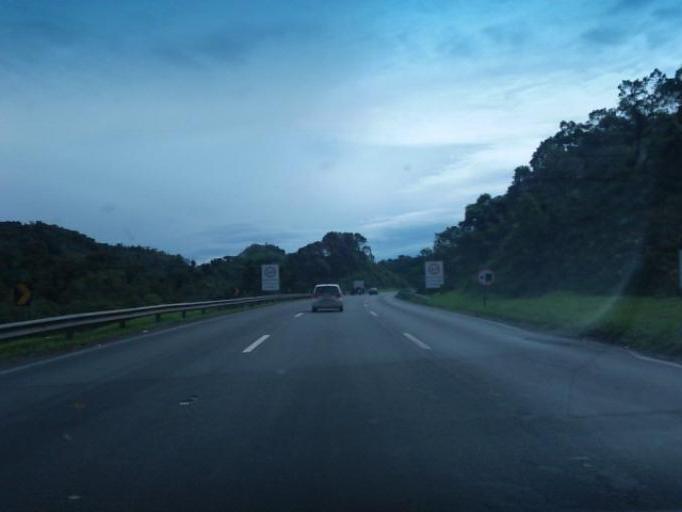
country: BR
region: Sao Paulo
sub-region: Cajati
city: Cajati
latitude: -24.9004
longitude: -48.2478
